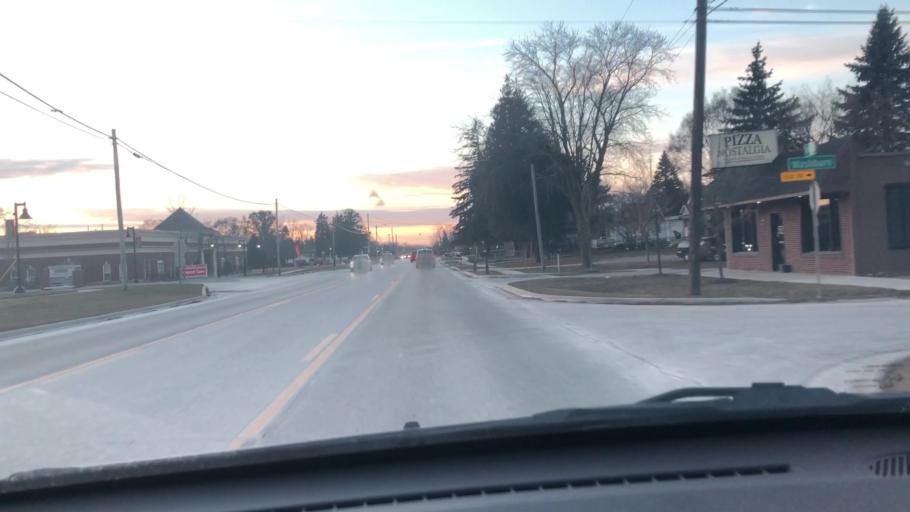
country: US
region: Michigan
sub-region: Macomb County
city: Shelby
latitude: 42.7203
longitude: -83.0356
